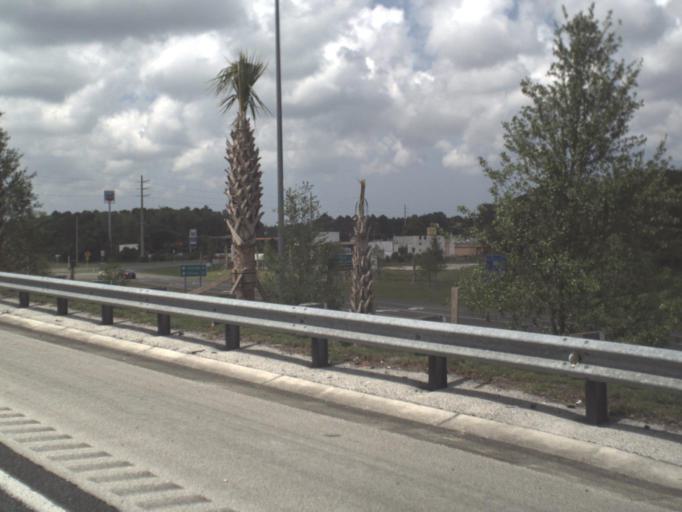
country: US
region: Florida
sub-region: Saint Johns County
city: Saint Augustine South
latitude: 29.8243
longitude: -81.3784
